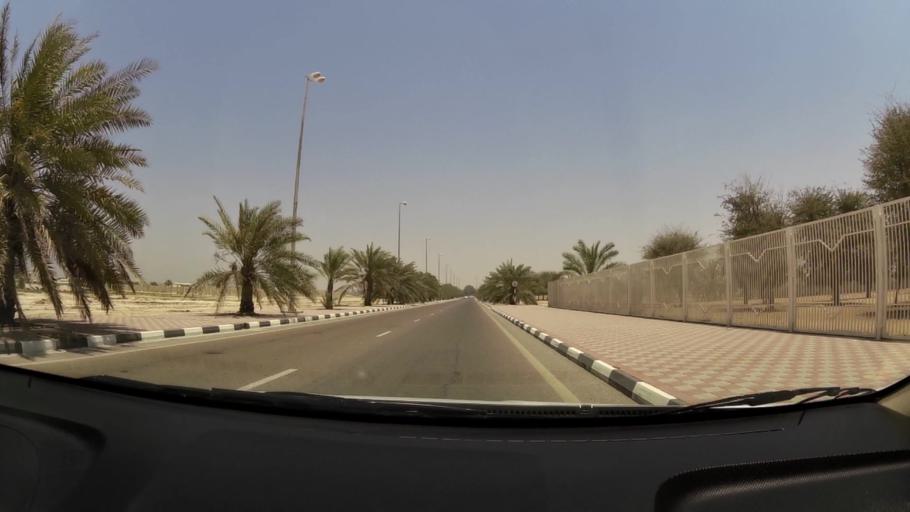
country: AE
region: Umm al Qaywayn
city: Umm al Qaywayn
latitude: 25.5309
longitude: 55.5322
